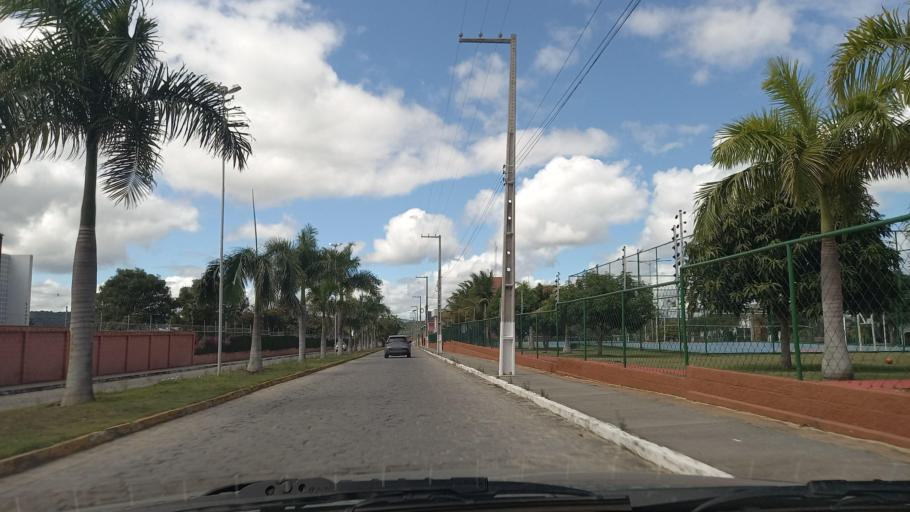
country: BR
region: Pernambuco
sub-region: Caruaru
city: Caruaru
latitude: -8.2484
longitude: -35.9521
